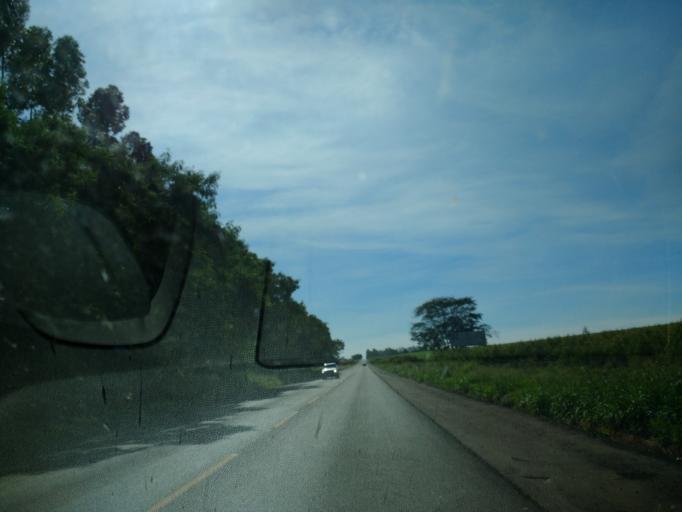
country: BR
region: Parana
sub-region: Umuarama
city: Umuarama
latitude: -23.8489
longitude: -53.3691
